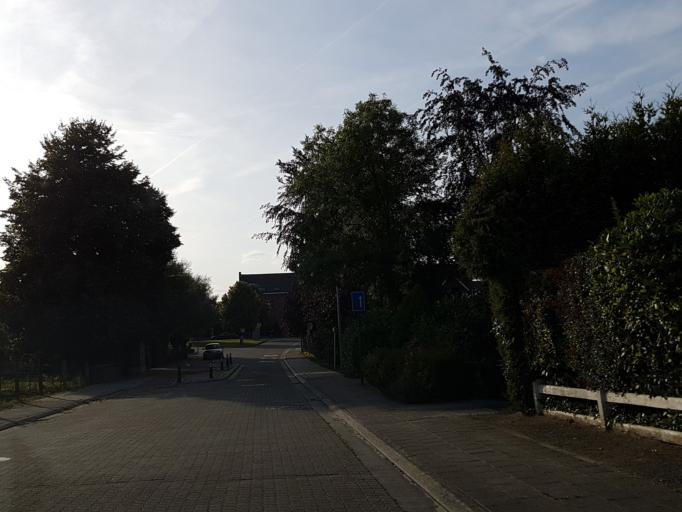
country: BE
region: Flanders
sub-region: Provincie Vlaams-Brabant
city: Opwijk
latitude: 50.9367
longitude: 4.1337
